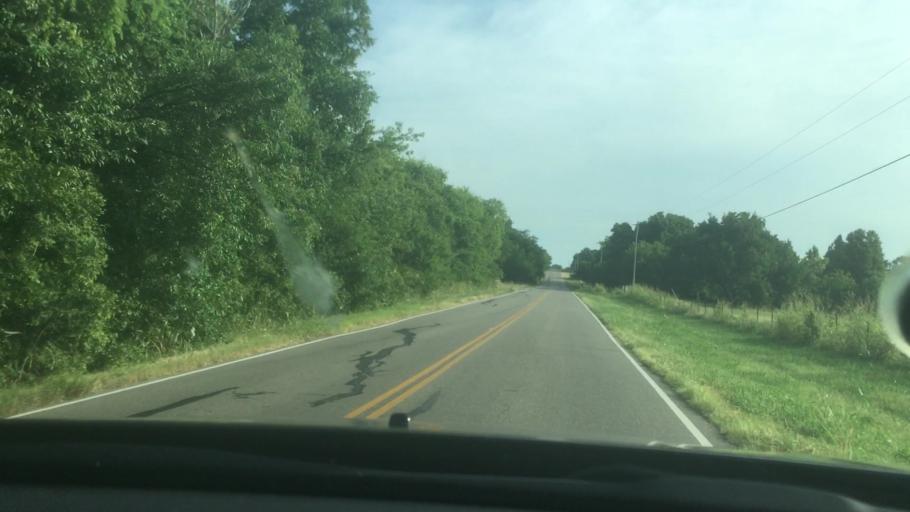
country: US
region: Oklahoma
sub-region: Pontotoc County
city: Ada
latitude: 34.7258
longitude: -96.6700
